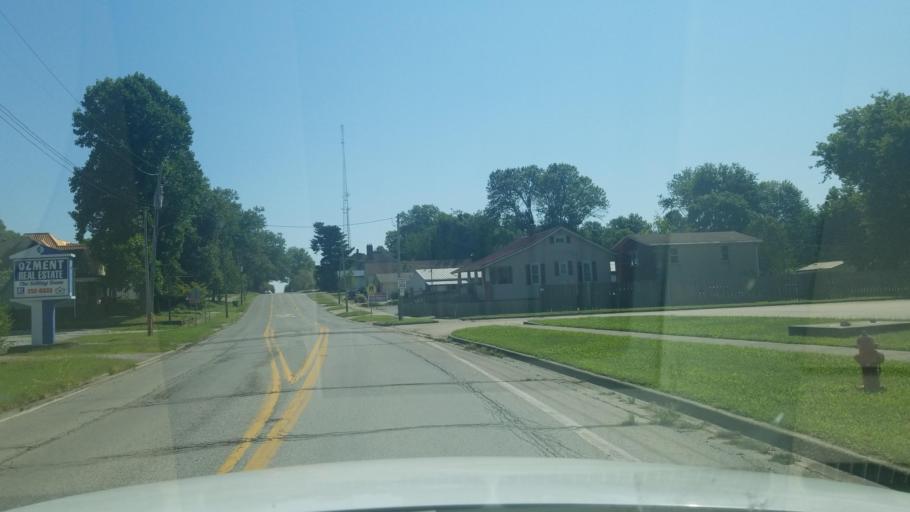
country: US
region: Illinois
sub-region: Saline County
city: Harrisburg
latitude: 37.7384
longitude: -88.5487
